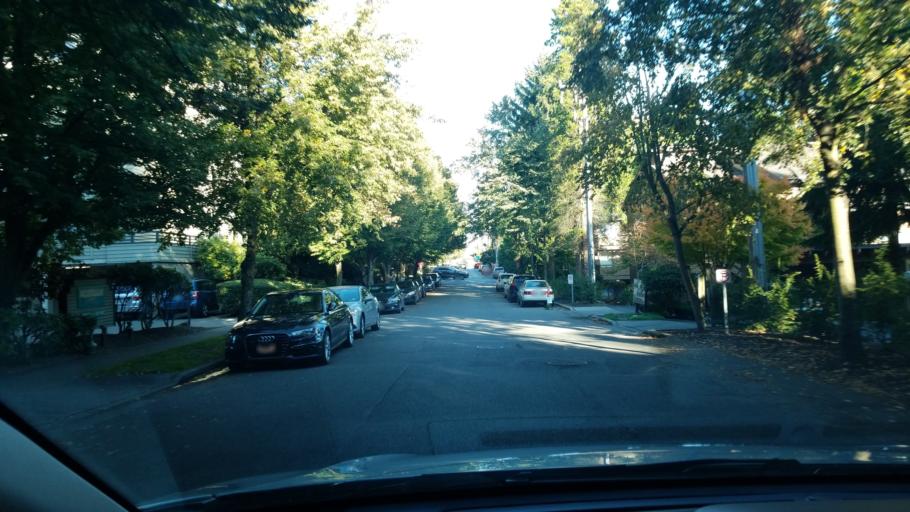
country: US
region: Washington
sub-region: King County
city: Shoreline
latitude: 47.7068
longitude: -122.3352
